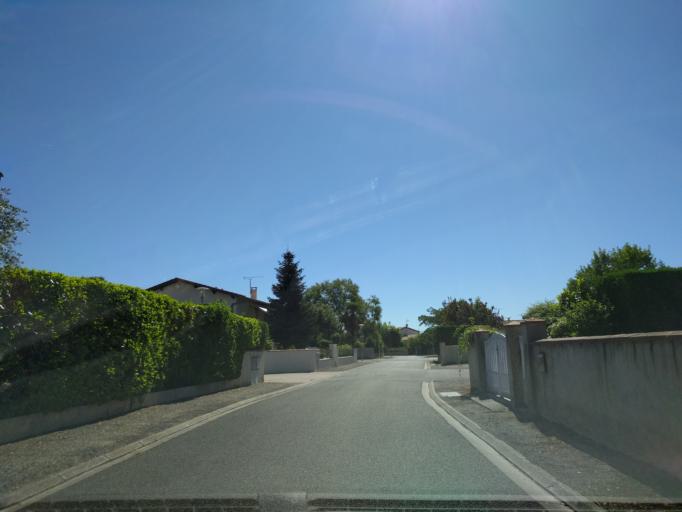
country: FR
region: Midi-Pyrenees
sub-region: Departement du Tarn-et-Garonne
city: Montauban
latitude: 44.0343
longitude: 1.3652
